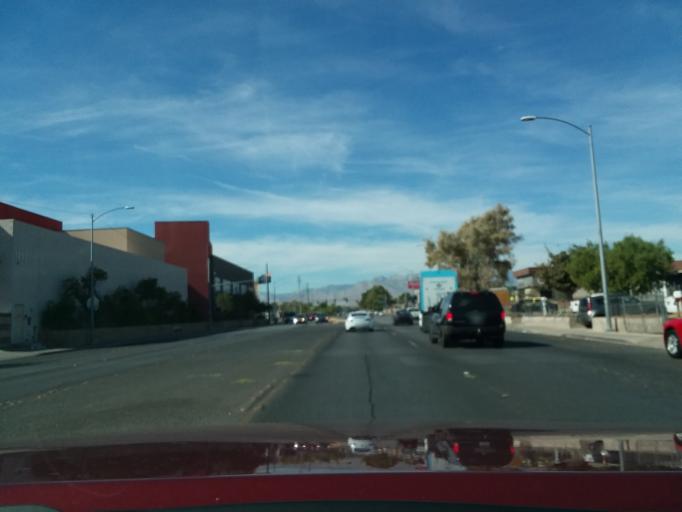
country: US
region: Nevada
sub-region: Clark County
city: Las Vegas
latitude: 36.1957
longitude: -115.1578
